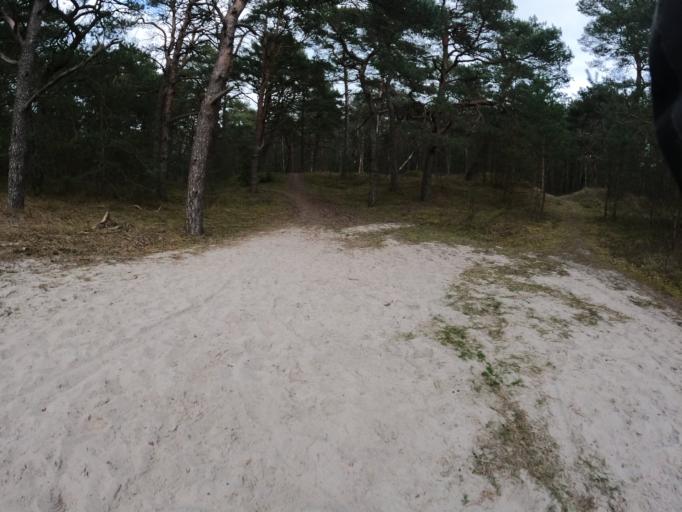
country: PL
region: West Pomeranian Voivodeship
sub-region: Powiat gryficki
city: Mrzezyno
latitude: 54.1349
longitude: 15.2536
